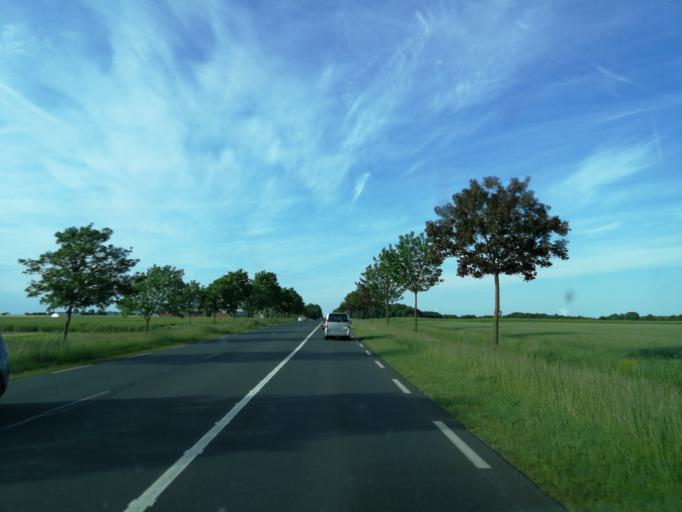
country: FR
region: Centre
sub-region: Departement d'Eure-et-Loir
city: Bonneval
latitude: 48.1620
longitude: 1.3622
